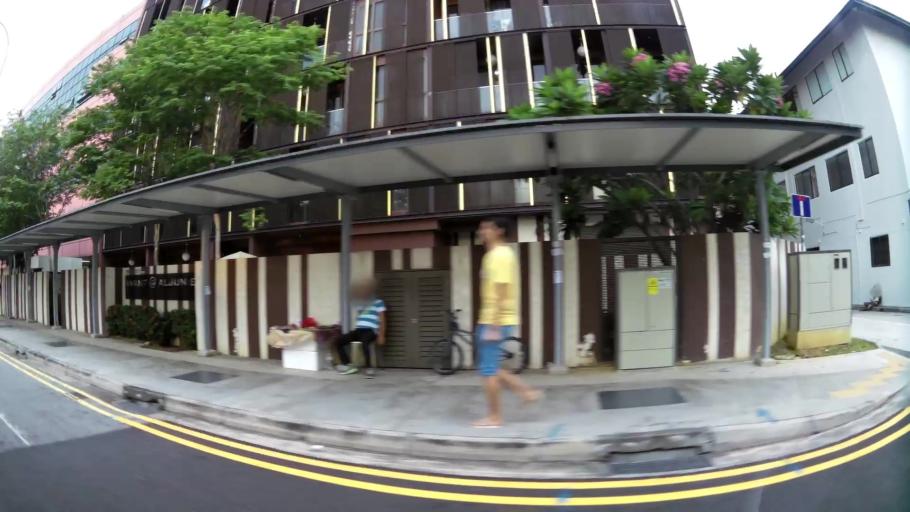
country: SG
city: Singapore
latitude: 1.3135
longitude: 103.8822
